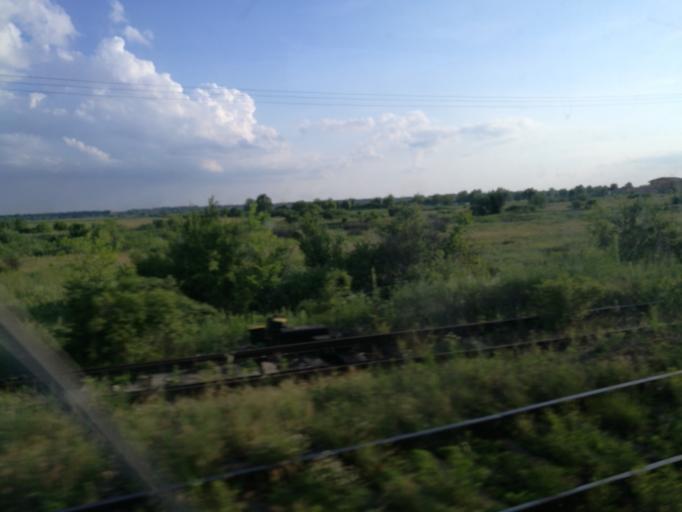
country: RO
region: Arges
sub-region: Comuna Calinesti
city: Calinesti
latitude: 44.8124
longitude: 25.0559
